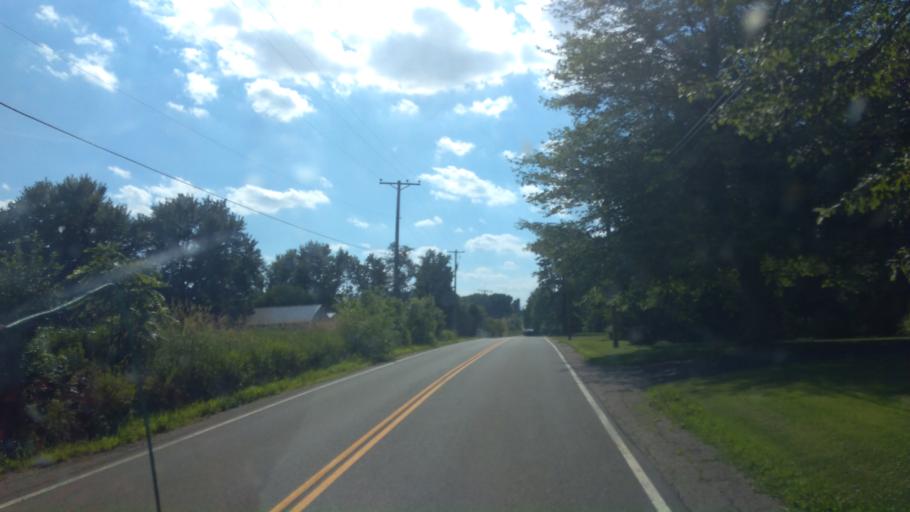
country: US
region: Ohio
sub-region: Stark County
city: Brewster
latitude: 40.7269
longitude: -81.5661
